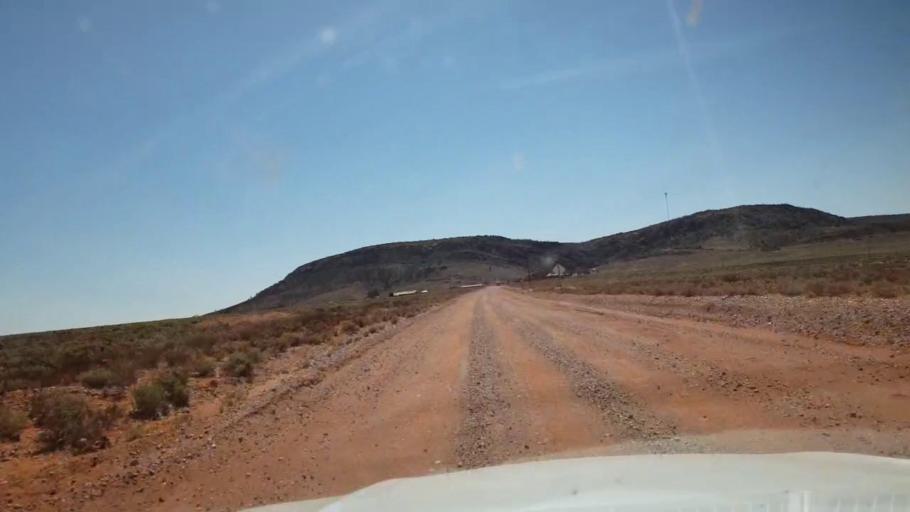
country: AU
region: South Australia
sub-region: Whyalla
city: Whyalla
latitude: -32.6921
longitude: 137.1292
